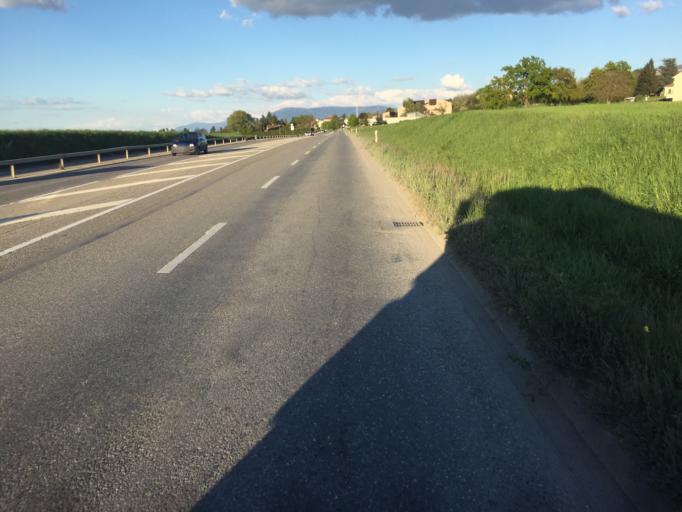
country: CH
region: Geneva
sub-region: Geneva
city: Bernex
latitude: 46.1746
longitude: 6.0581
